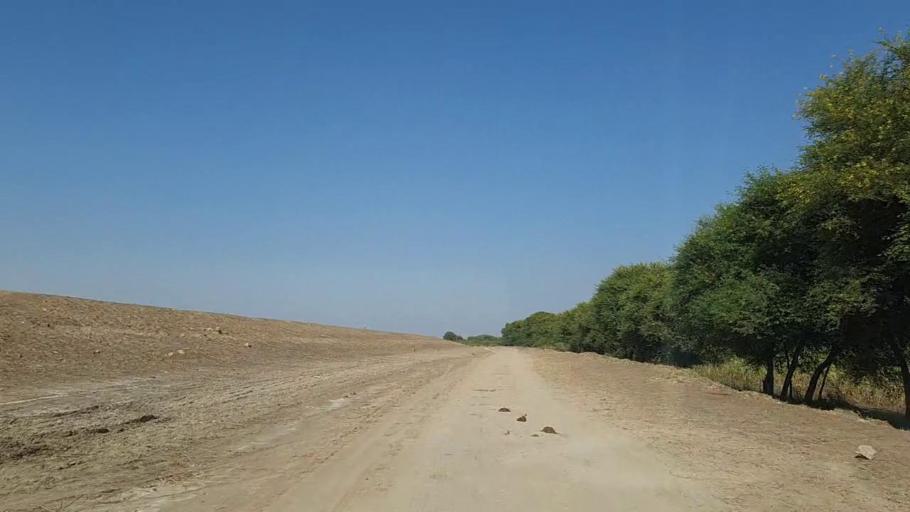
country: PK
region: Sindh
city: Chuhar Jamali
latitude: 24.5343
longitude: 68.0152
